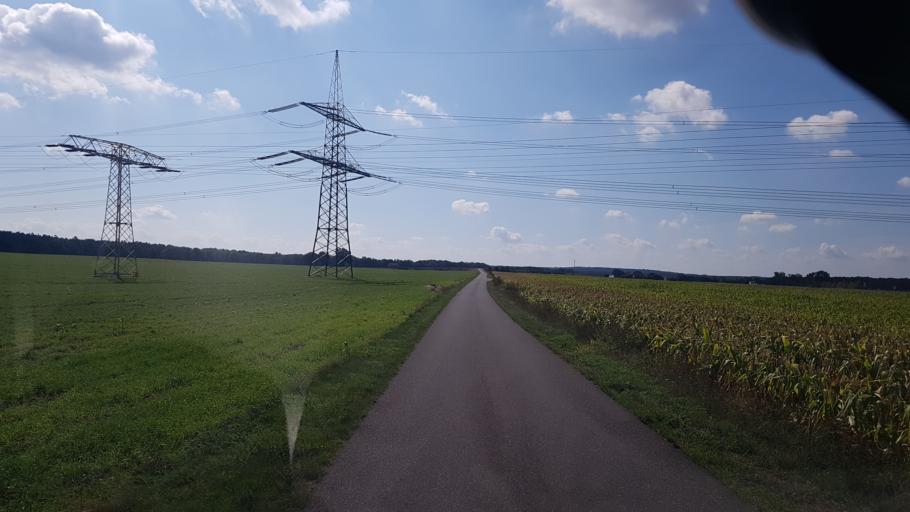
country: DE
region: Brandenburg
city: Drebkau
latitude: 51.6602
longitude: 14.2460
